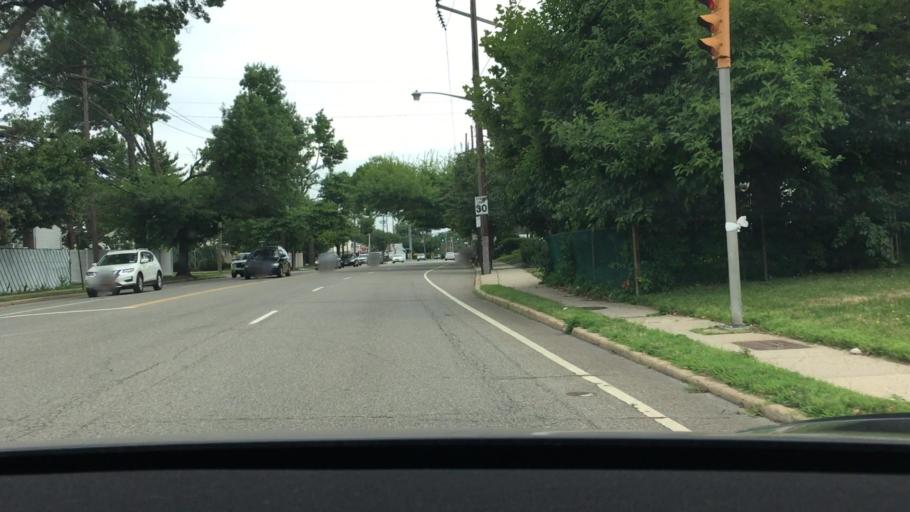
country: US
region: New York
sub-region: Nassau County
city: North New Hyde Park
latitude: 40.7449
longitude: -73.6954
